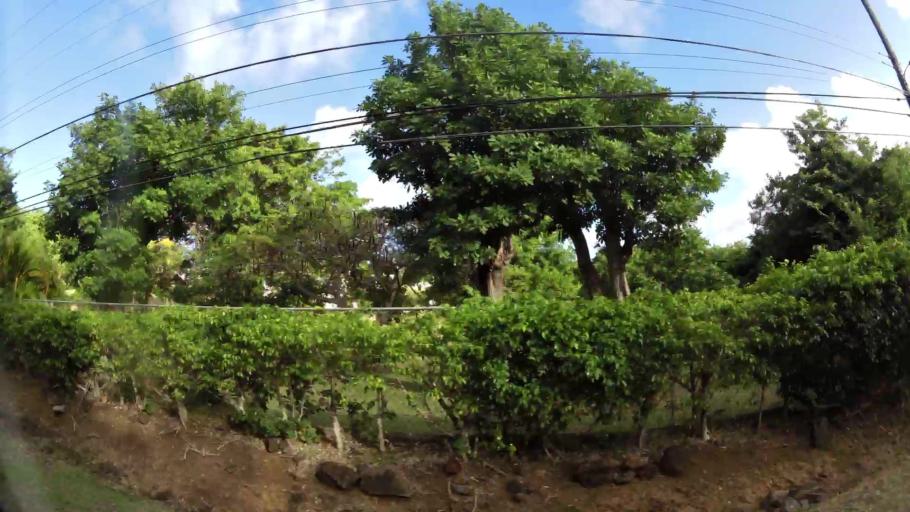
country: LC
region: Gros-Islet
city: Gros Islet
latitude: 14.1011
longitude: -60.9434
